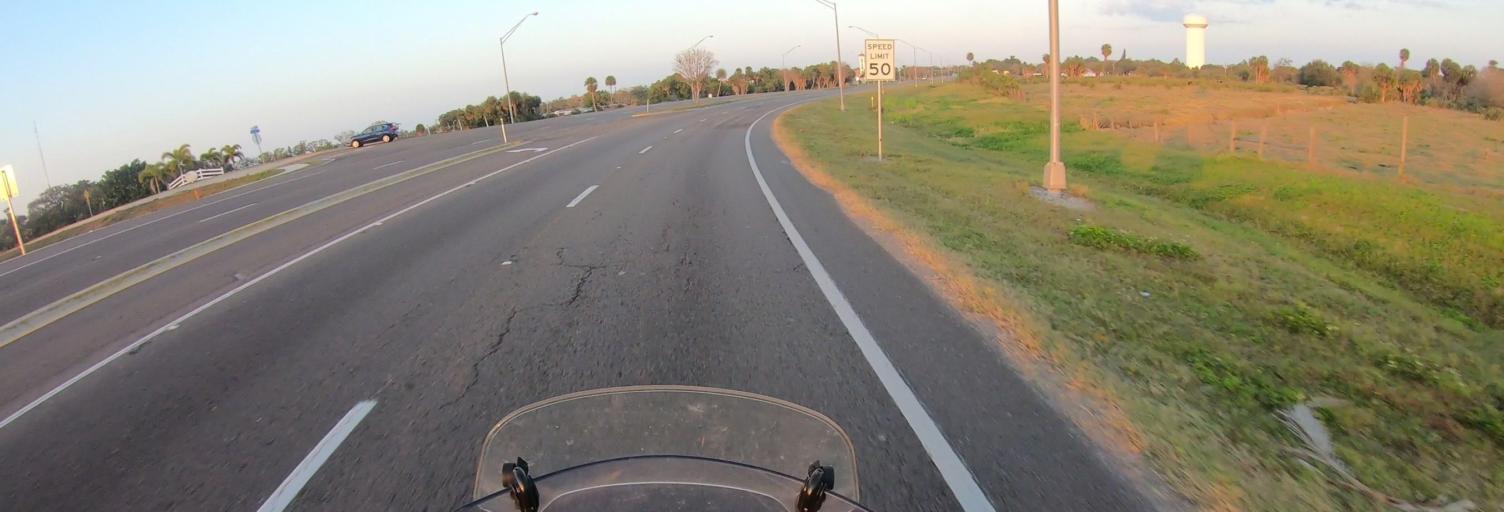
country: US
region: Florida
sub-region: Manatee County
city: Memphis
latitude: 27.5332
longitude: -82.5716
